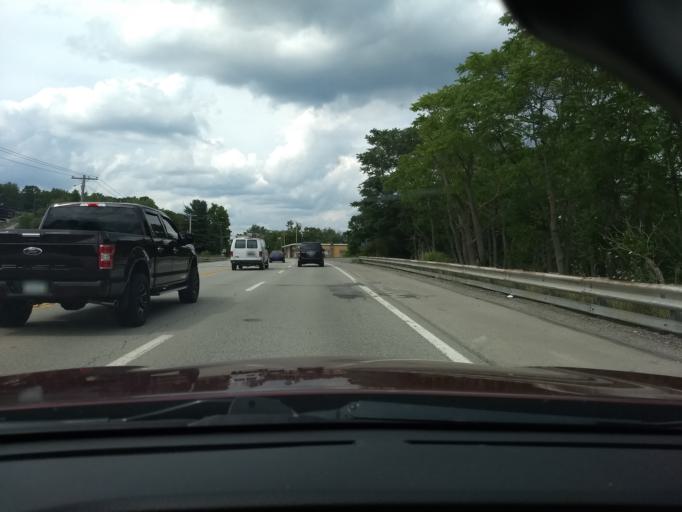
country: US
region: Pennsylvania
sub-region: Armstrong County
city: Freeport
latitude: 40.6544
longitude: -79.7075
